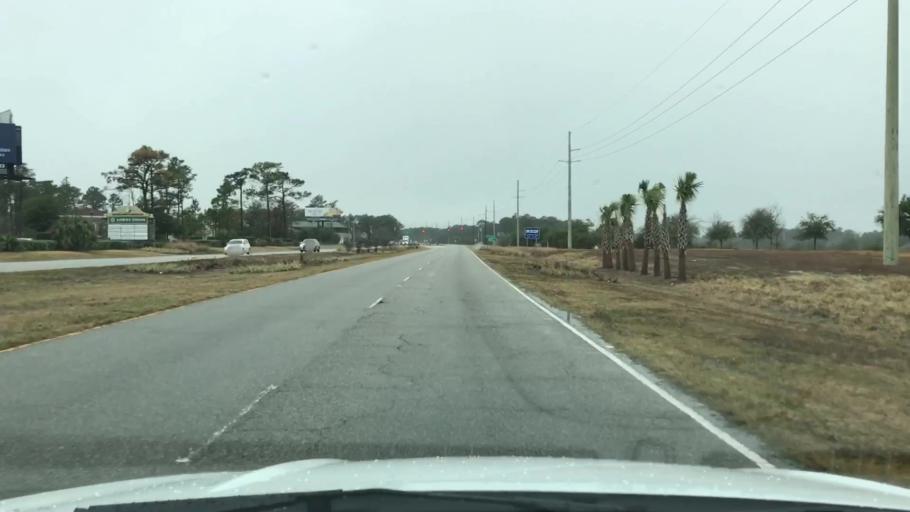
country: US
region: South Carolina
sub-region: Horry County
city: Myrtle Beach
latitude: 33.7628
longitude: -78.8142
